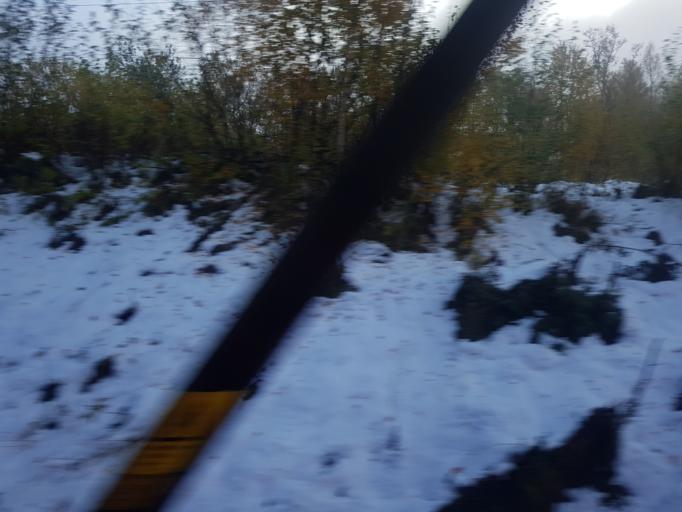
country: NO
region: Sor-Trondelag
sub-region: Oppdal
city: Oppdal
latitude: 62.5754
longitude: 9.6509
